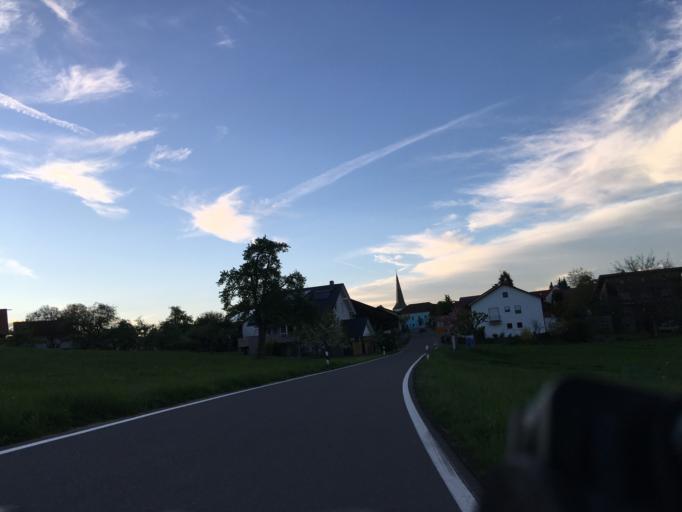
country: DE
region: Baden-Wuerttemberg
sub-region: Freiburg Region
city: Gailingen
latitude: 47.7203
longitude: 8.7566
